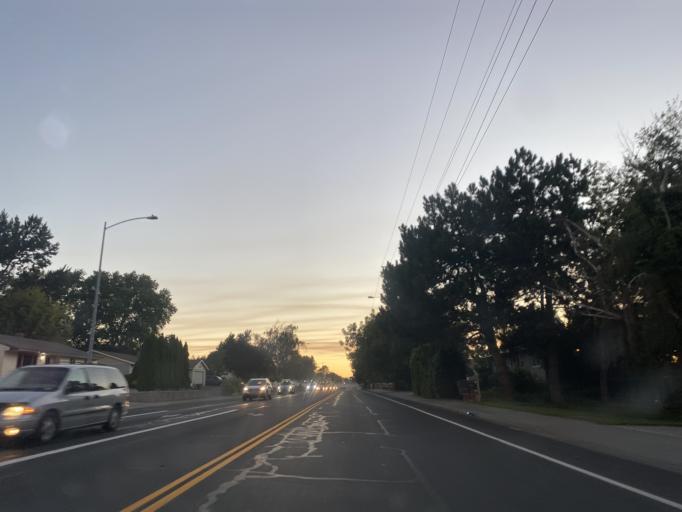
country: US
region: Washington
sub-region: Benton County
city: Kennewick
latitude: 46.1986
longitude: -119.1485
